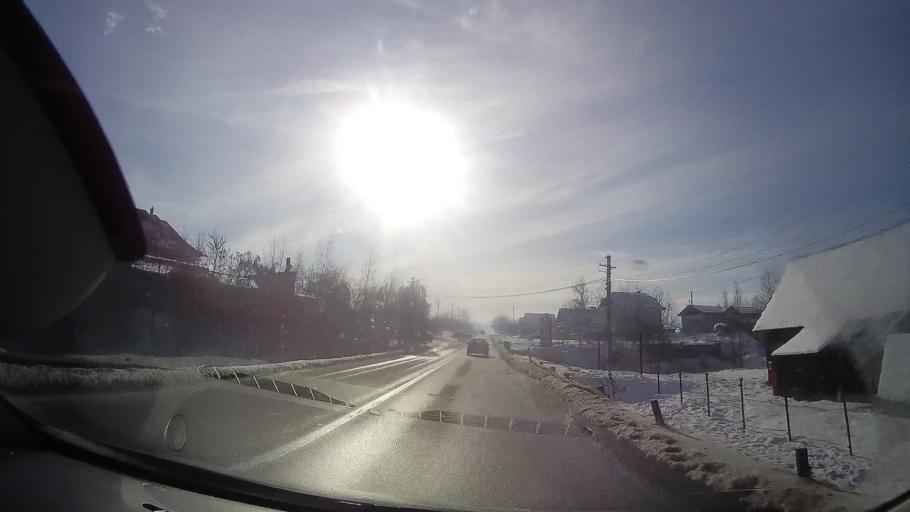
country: RO
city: Vanatori-Neamt
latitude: 47.1816
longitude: 26.3309
